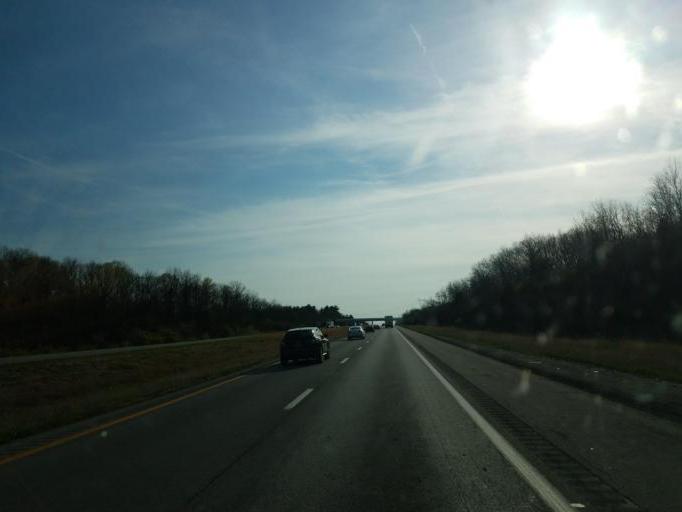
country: US
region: Ohio
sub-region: Franklin County
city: Grove City
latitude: 39.8156
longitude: -83.1826
